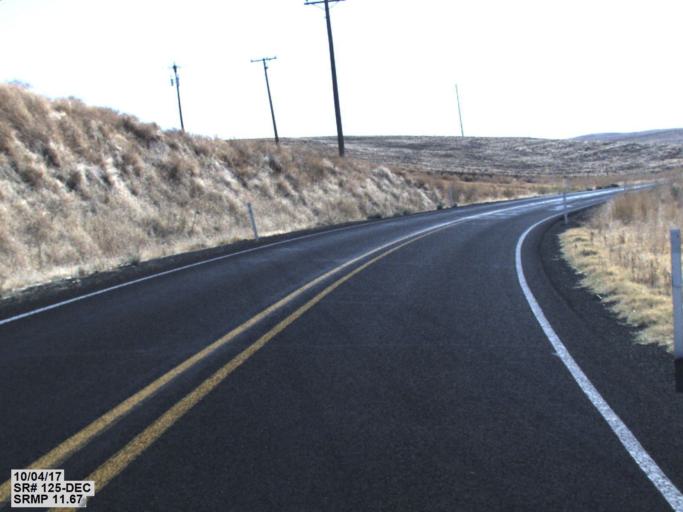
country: US
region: Washington
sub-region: Walla Walla County
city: Walla Walla
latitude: 46.1407
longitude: -118.3727
